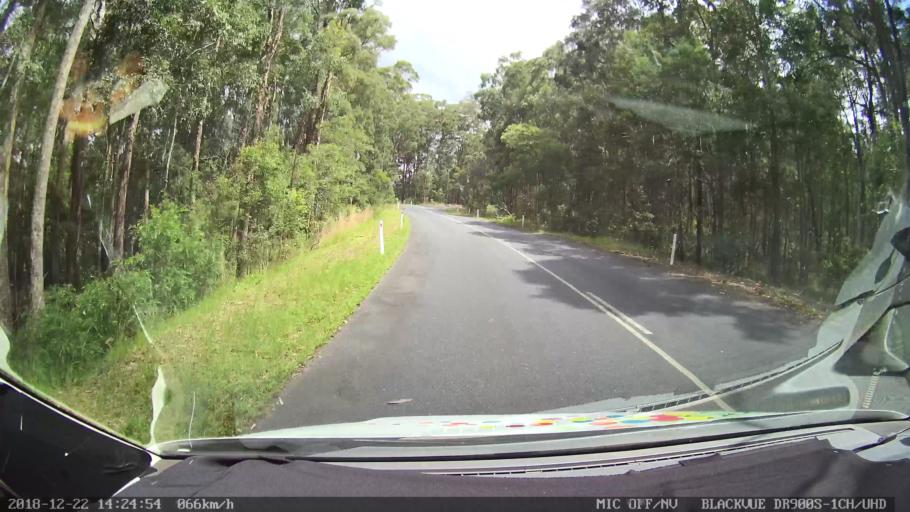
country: AU
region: New South Wales
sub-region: Bellingen
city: Dorrigo
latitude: -30.0478
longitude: 152.6420
